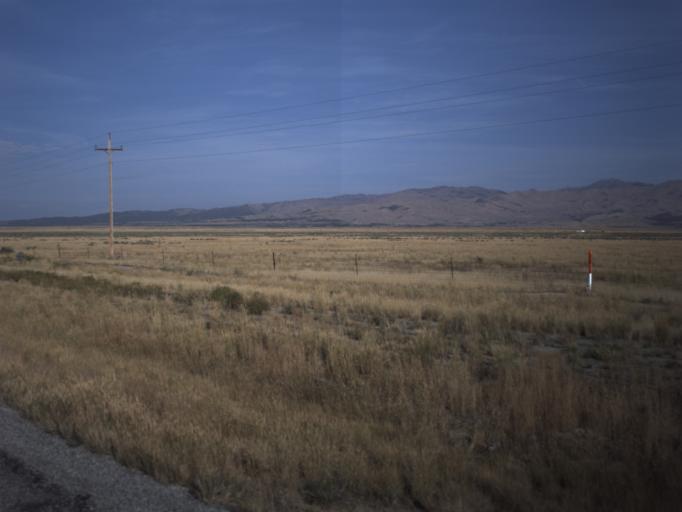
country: US
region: Idaho
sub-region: Oneida County
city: Malad City
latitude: 41.9661
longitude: -112.9667
